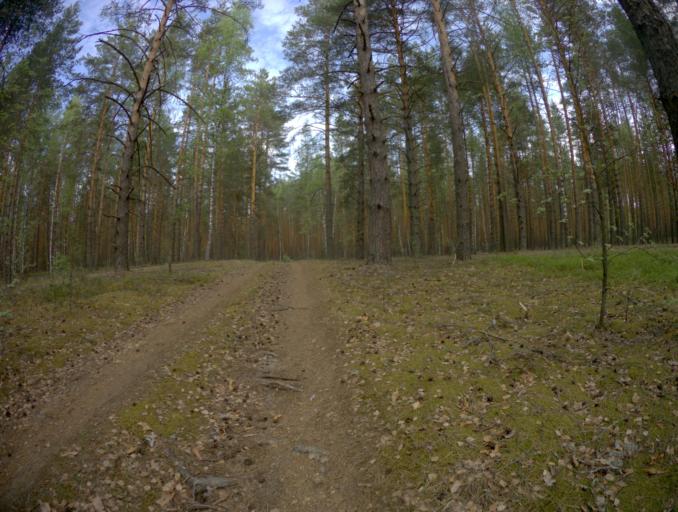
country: RU
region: Ivanovo
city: Talitsy
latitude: 56.4853
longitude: 42.1652
